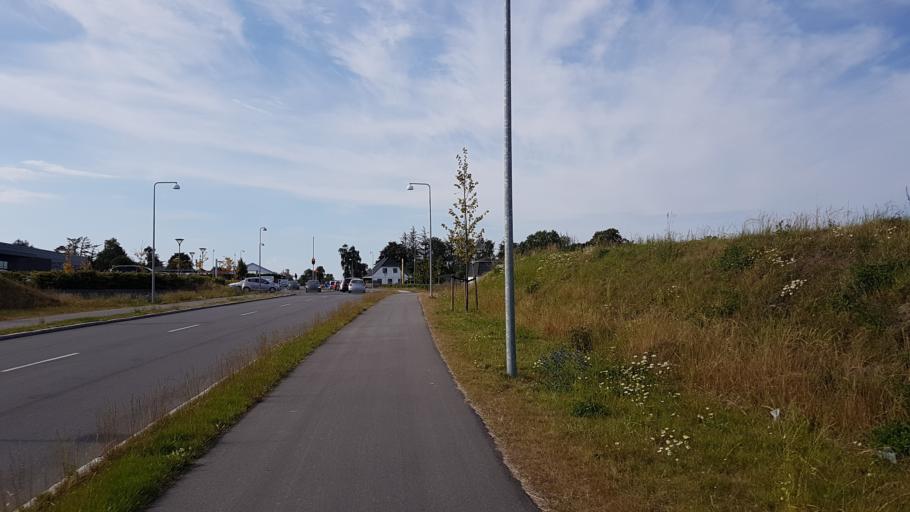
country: DK
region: Zealand
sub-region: Roskilde Kommune
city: Jyllinge
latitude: 55.7626
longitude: 12.1188
